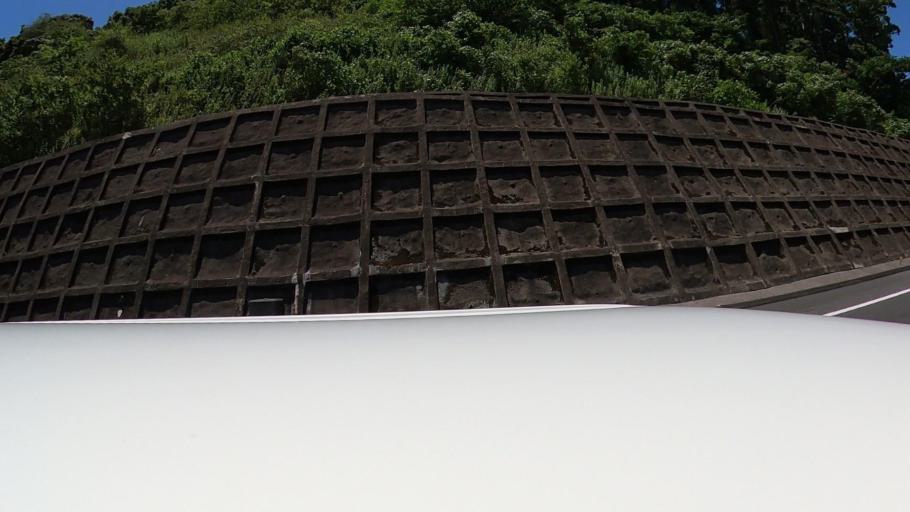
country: JP
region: Miyazaki
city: Nobeoka
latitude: 32.4030
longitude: 131.6154
